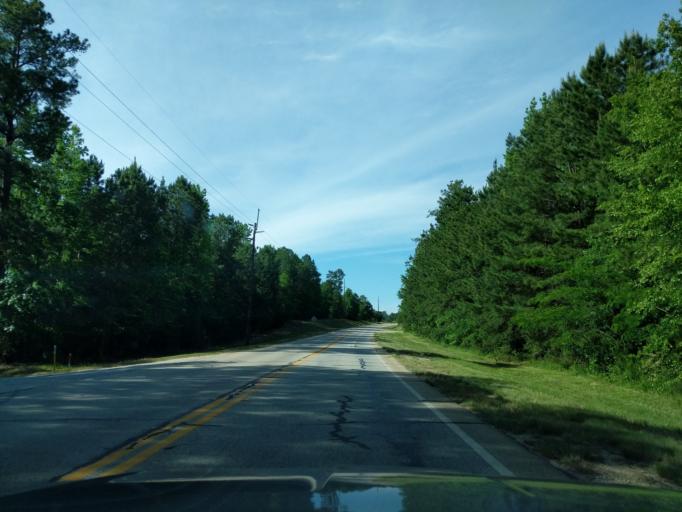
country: US
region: Georgia
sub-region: Jefferson County
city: Wrens
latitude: 33.2747
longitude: -82.3868
